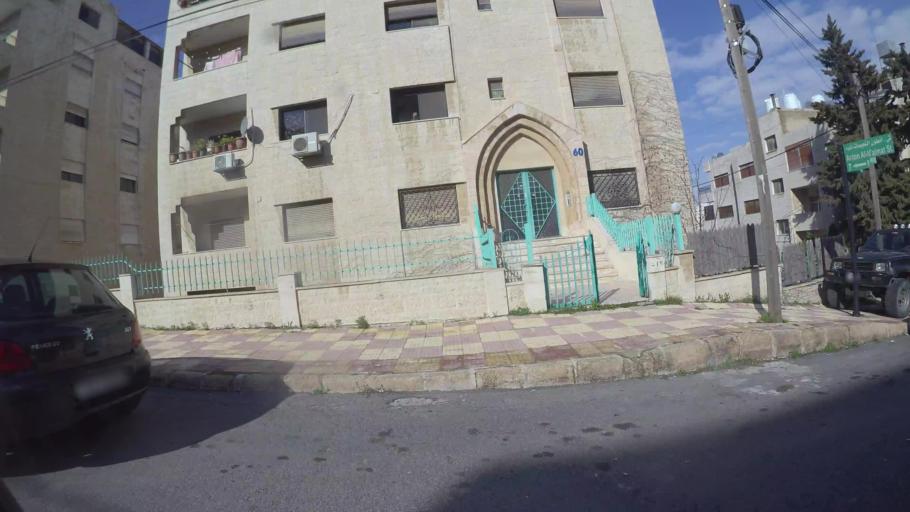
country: JO
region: Amman
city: Al Jubayhah
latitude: 32.0198
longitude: 35.8593
